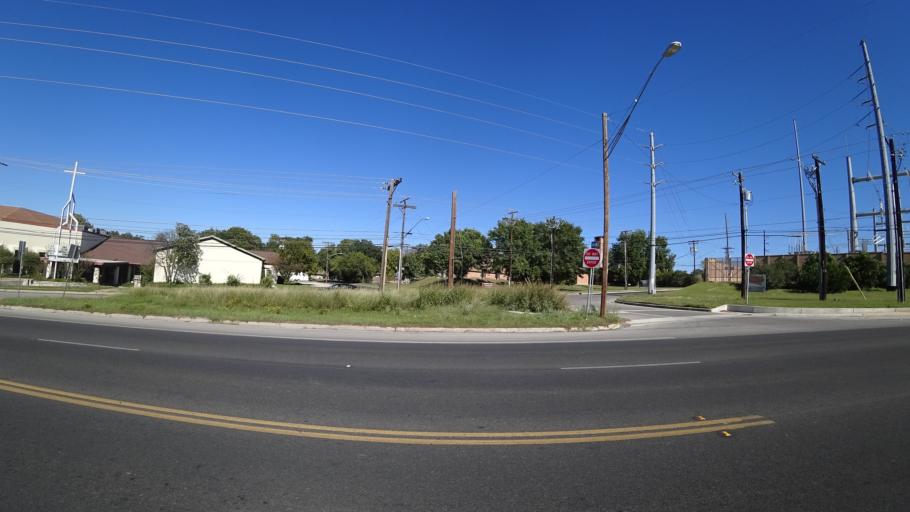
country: US
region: Texas
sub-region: Travis County
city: Austin
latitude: 30.3287
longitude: -97.7278
